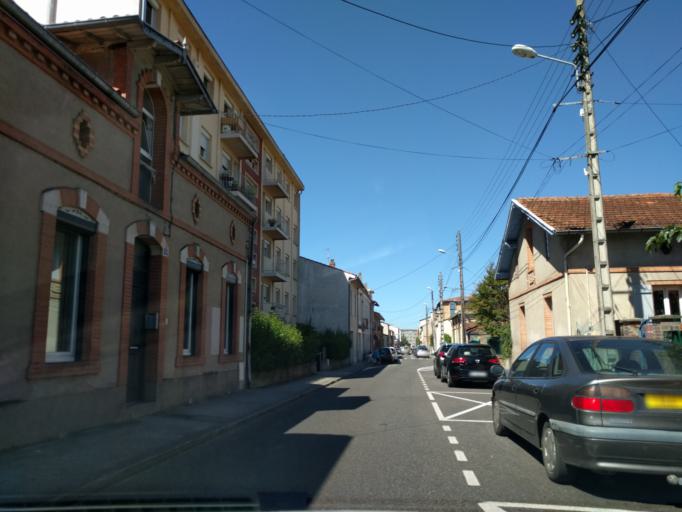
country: FR
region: Midi-Pyrenees
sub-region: Departement du Tarn-et-Garonne
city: Montauban
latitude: 44.0179
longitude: 1.3662
